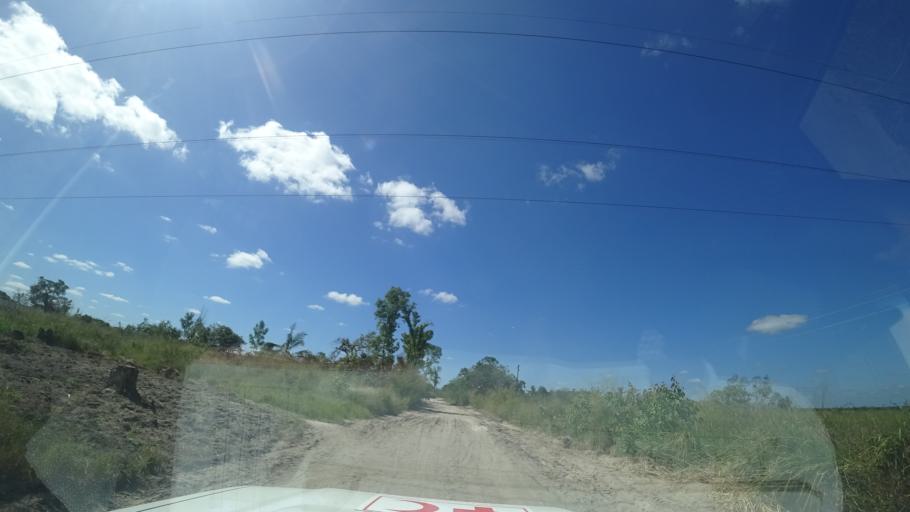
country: MZ
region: Sofala
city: Dondo
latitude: -19.5055
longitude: 34.6105
